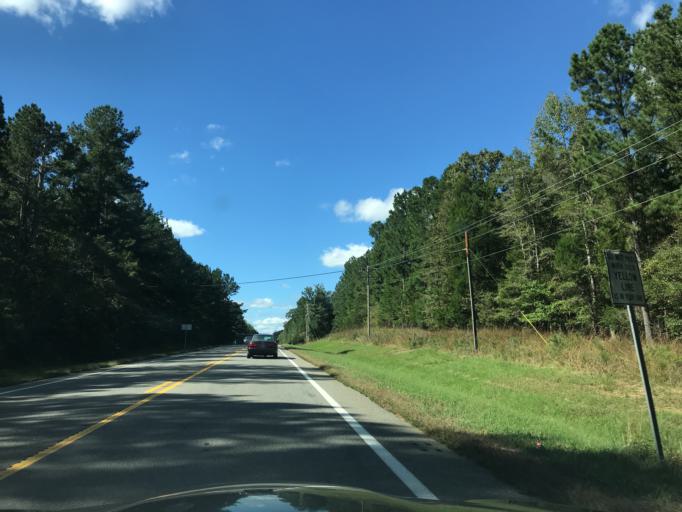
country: US
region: North Carolina
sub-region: Durham County
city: Gorman
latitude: 35.9813
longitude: -78.7477
